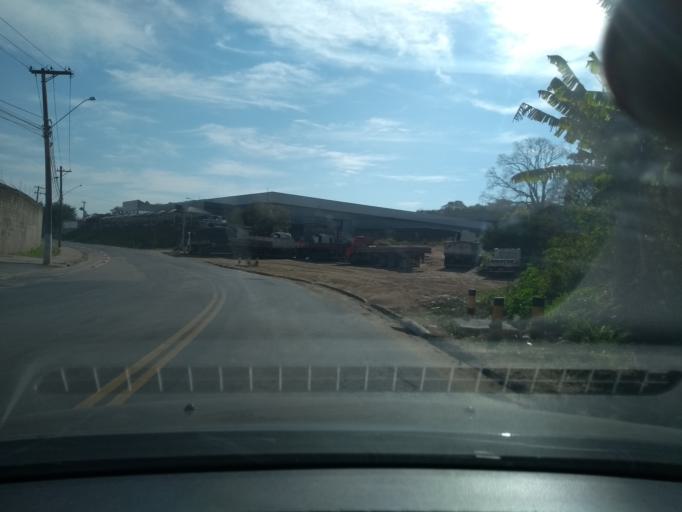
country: BR
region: Sao Paulo
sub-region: Itupeva
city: Itupeva
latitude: -23.1488
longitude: -47.0440
